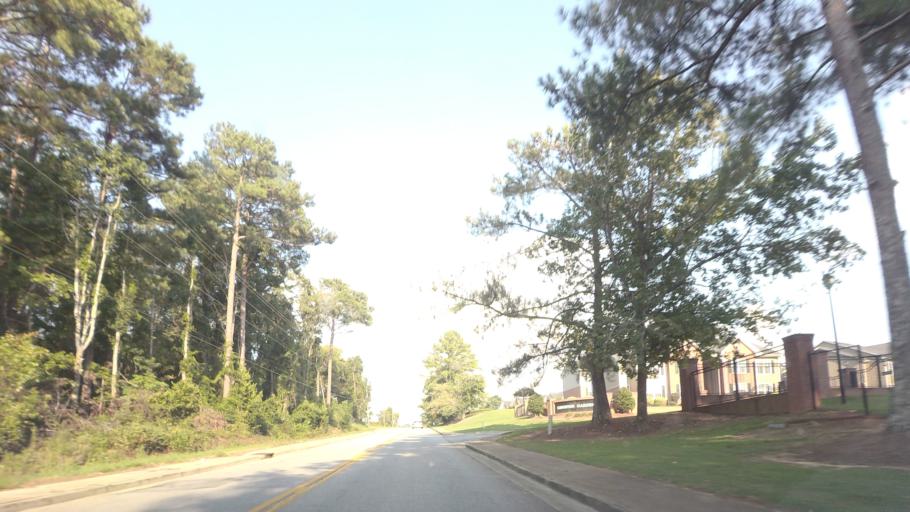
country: US
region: Georgia
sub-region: Bibb County
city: Macon
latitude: 32.8472
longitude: -83.6989
